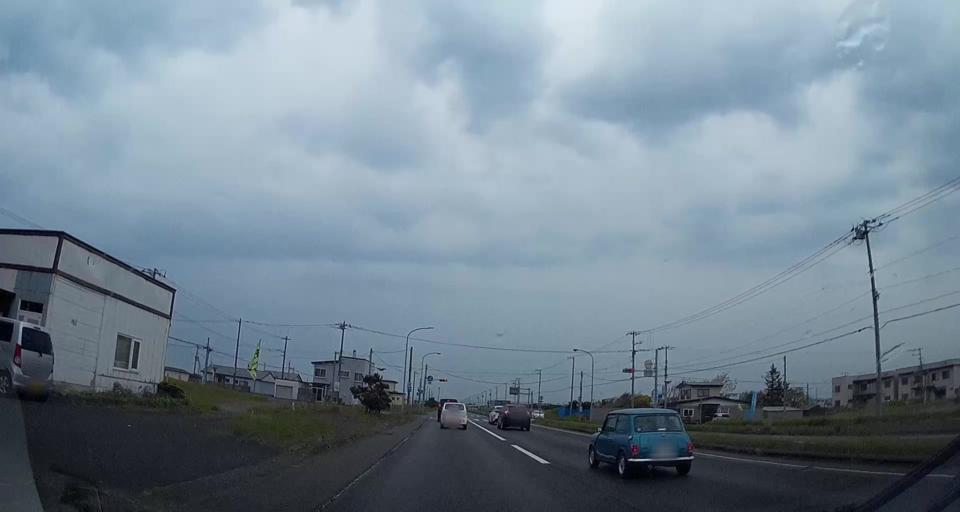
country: JP
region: Hokkaido
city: Tomakomai
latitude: 42.6039
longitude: 141.4941
